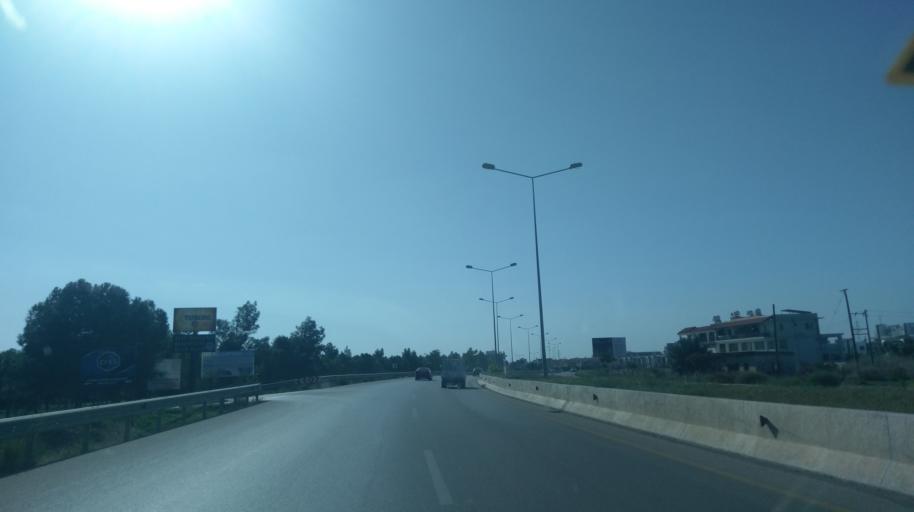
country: CY
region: Ammochostos
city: Trikomo
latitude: 35.2008
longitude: 33.8946
